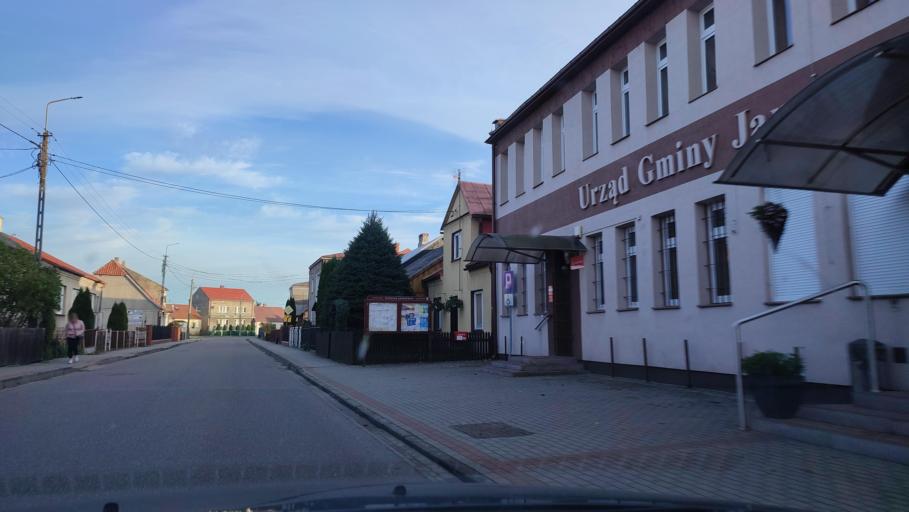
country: PL
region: Masovian Voivodeship
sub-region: Powiat mlawski
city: Dzierzgowo
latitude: 53.3166
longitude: 20.6712
